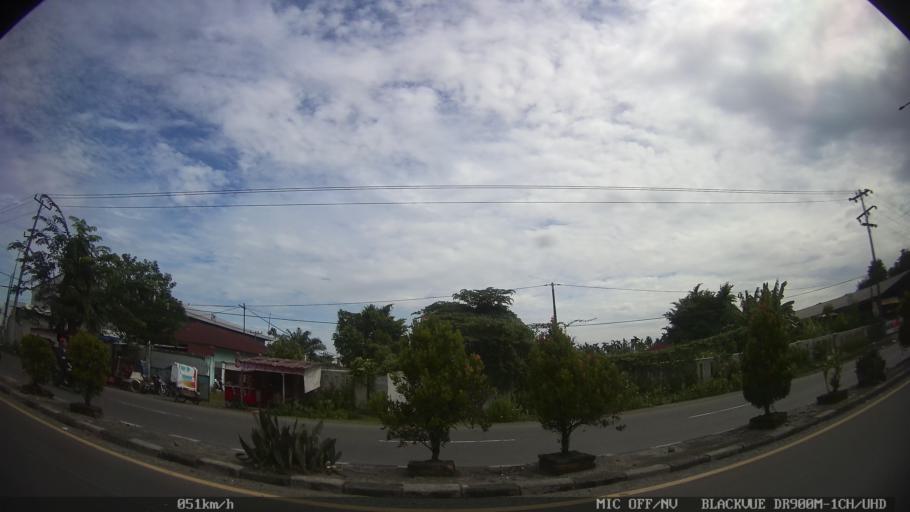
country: ID
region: North Sumatra
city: Sunggal
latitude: 3.5994
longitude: 98.5868
